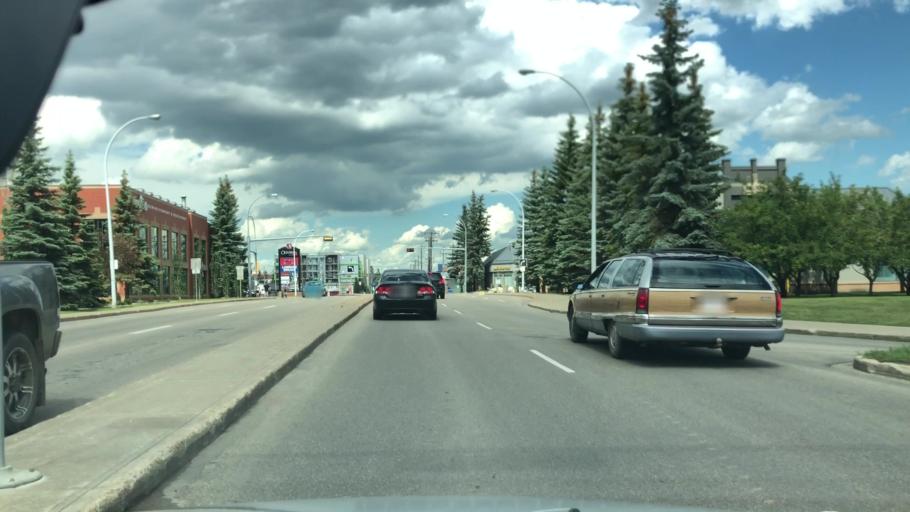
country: CA
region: Alberta
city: Edmonton
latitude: 53.5463
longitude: -113.5213
